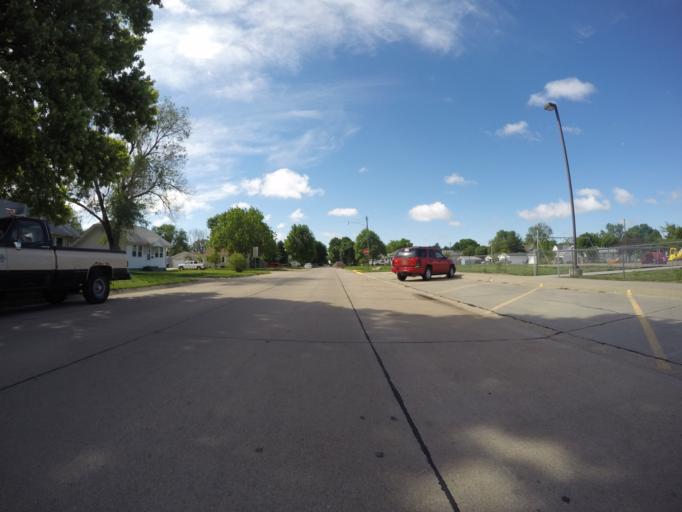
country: US
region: Nebraska
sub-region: Buffalo County
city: Kearney
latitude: 40.6898
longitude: -99.0874
